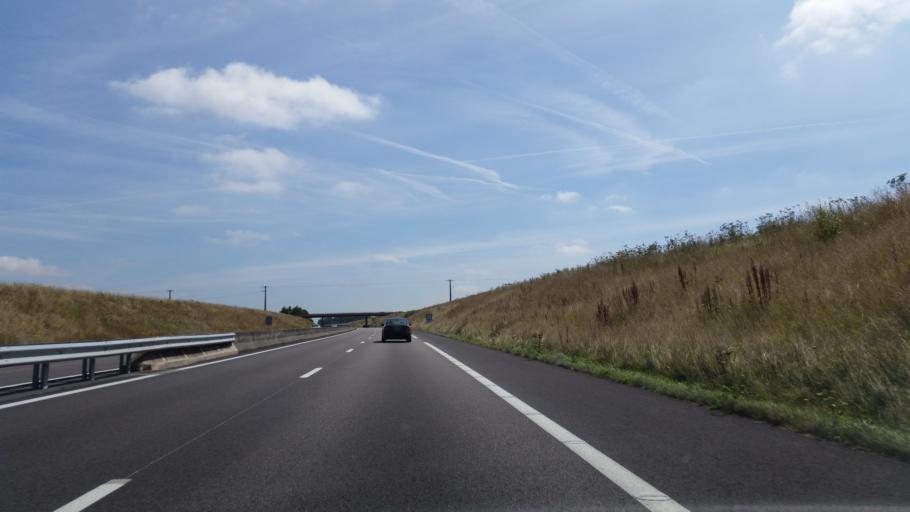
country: FR
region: Haute-Normandie
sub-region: Departement de la Seine-Maritime
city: Gaillefontaine
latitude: 49.7384
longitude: 1.6134
